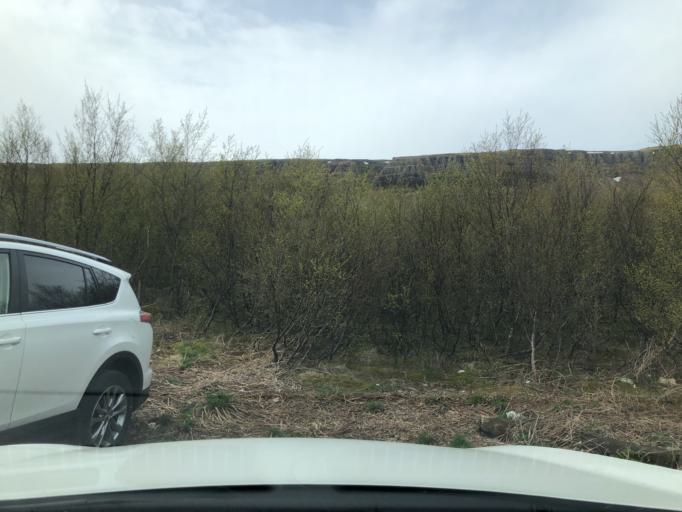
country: IS
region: South
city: Hveragerdi
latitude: 64.3852
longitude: -21.2939
